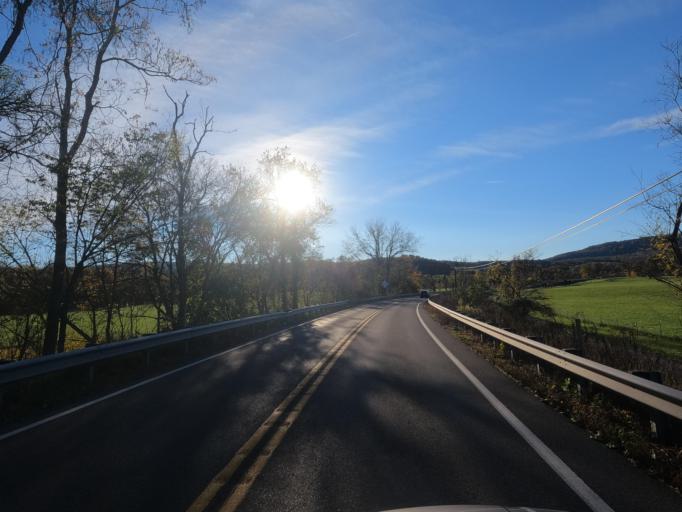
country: US
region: West Virginia
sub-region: Morgan County
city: Berkeley Springs
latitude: 39.5426
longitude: -78.4565
